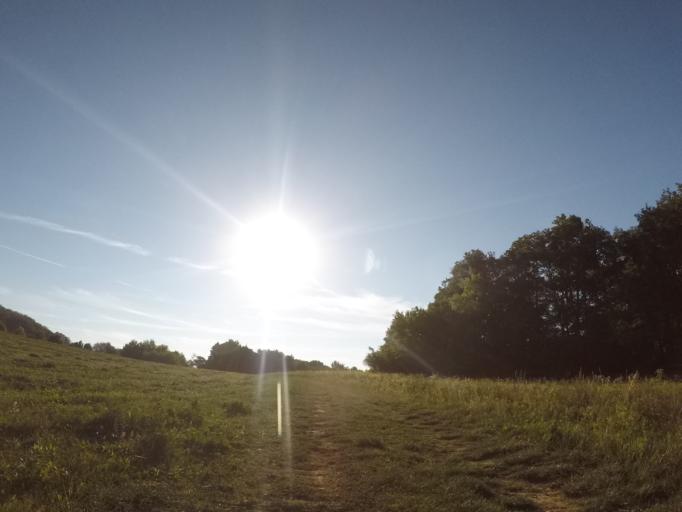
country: SK
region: Kosicky
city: Kosice
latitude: 48.7321
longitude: 21.1921
